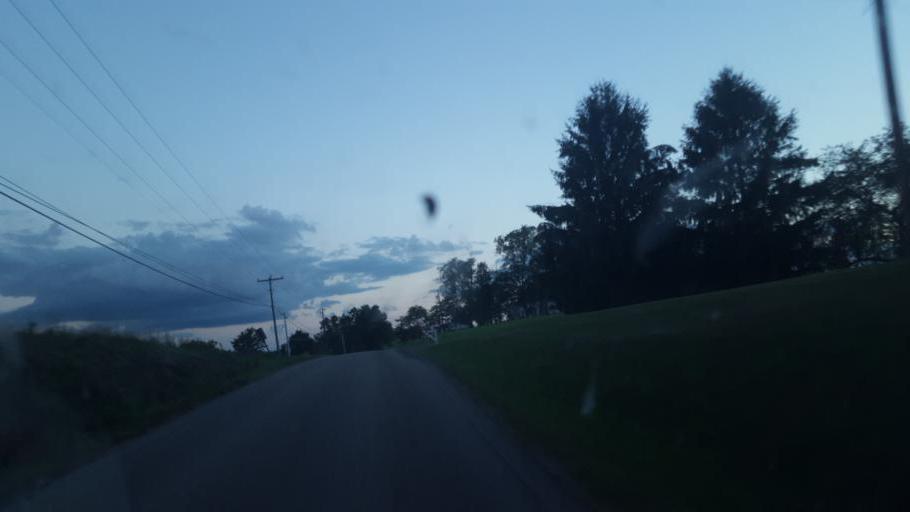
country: US
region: Pennsylvania
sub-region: Clarion County
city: Knox
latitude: 41.2209
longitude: -79.5416
